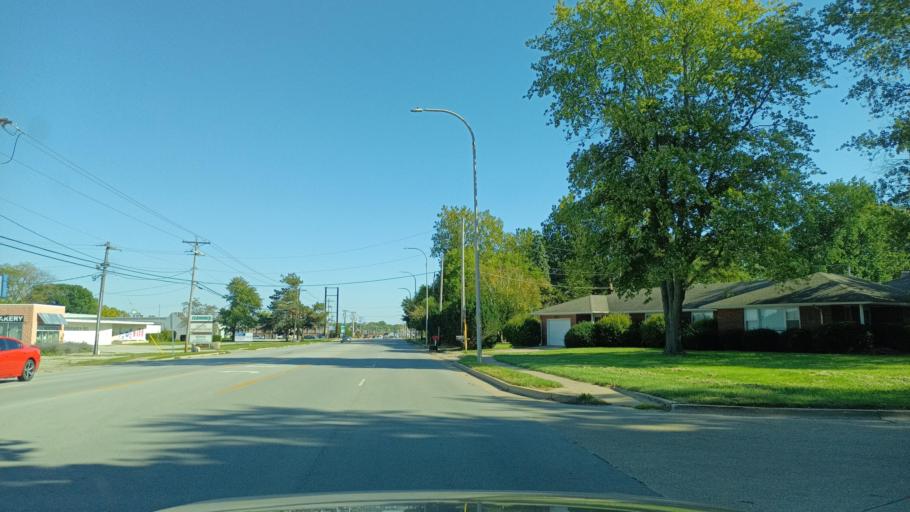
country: US
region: Illinois
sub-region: Champaign County
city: Champaign
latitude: 40.1351
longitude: -88.2647
